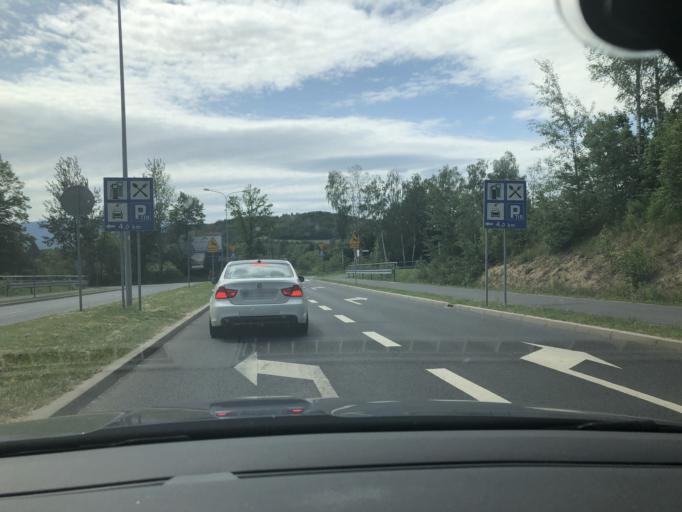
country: PL
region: Lower Silesian Voivodeship
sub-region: Jelenia Gora
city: Jelenia Gora
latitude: 50.8878
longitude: 15.7560
